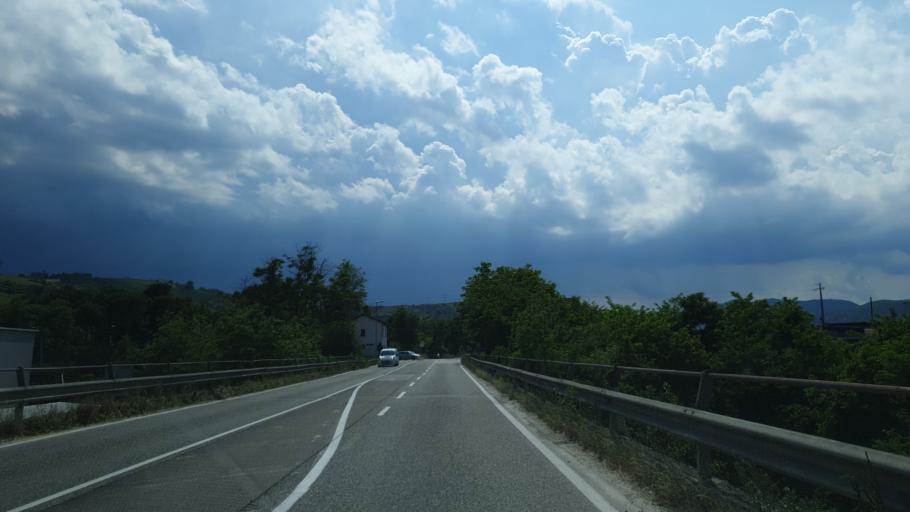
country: SM
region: Acquaviva
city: Acquaviva
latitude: 43.9600
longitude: 12.3995
